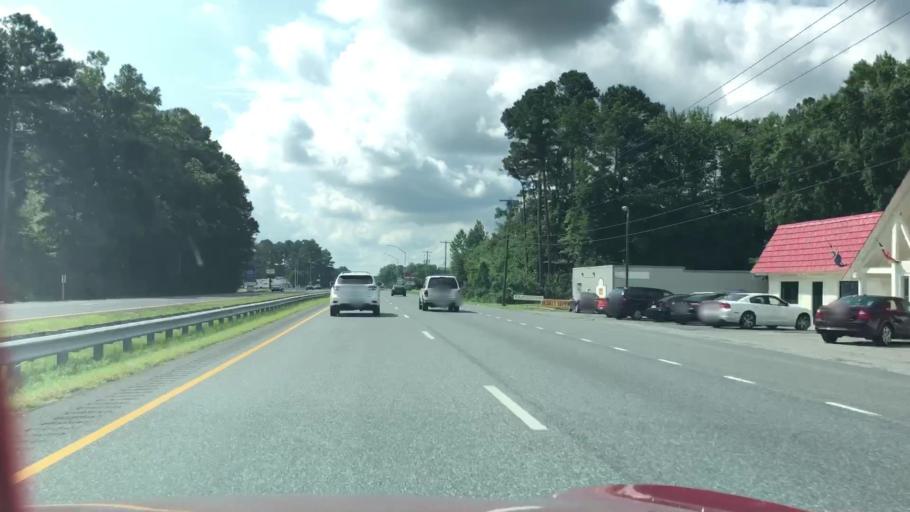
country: US
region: Maryland
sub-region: Worcester County
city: Pocomoke City
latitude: 38.0430
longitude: -75.5427
